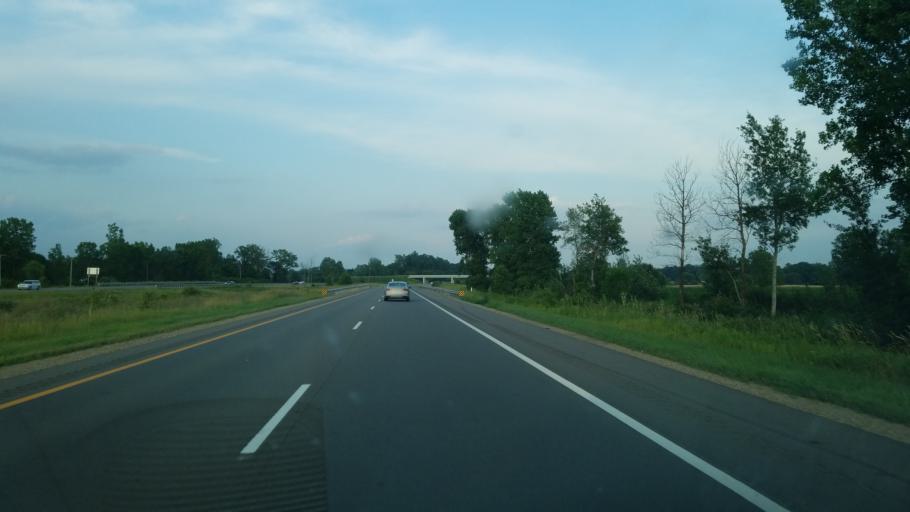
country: US
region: Michigan
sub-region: Livingston County
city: Fowlerville
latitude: 42.6498
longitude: -84.1213
